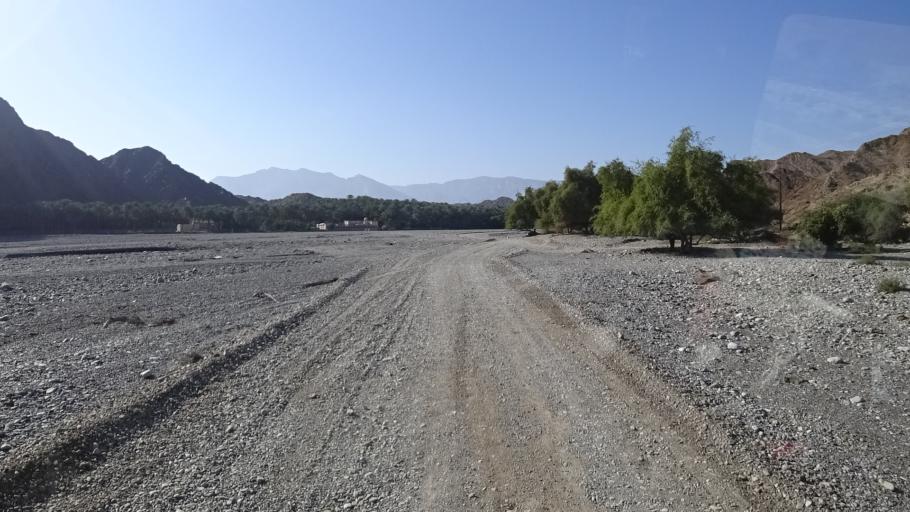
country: OM
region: Al Batinah
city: Bayt al `Awabi
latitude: 23.3934
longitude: 57.6628
